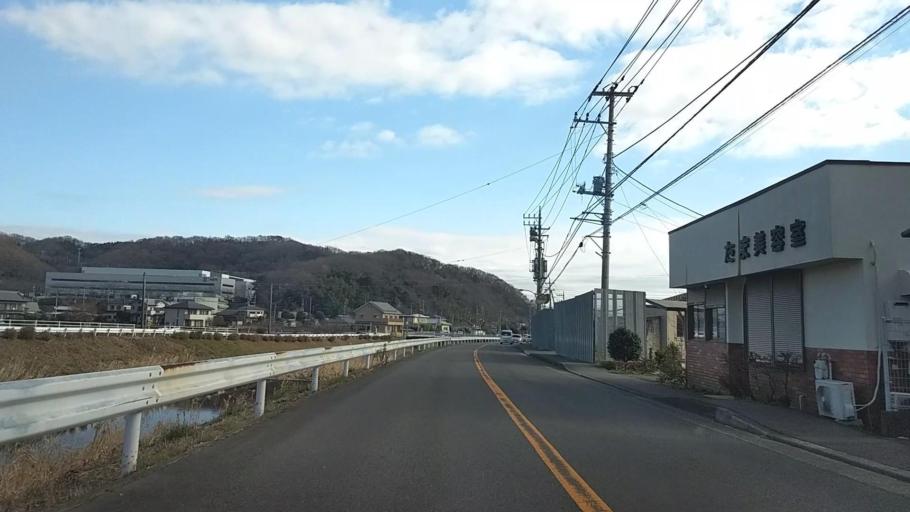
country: JP
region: Kanagawa
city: Isehara
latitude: 35.4353
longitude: 139.3103
